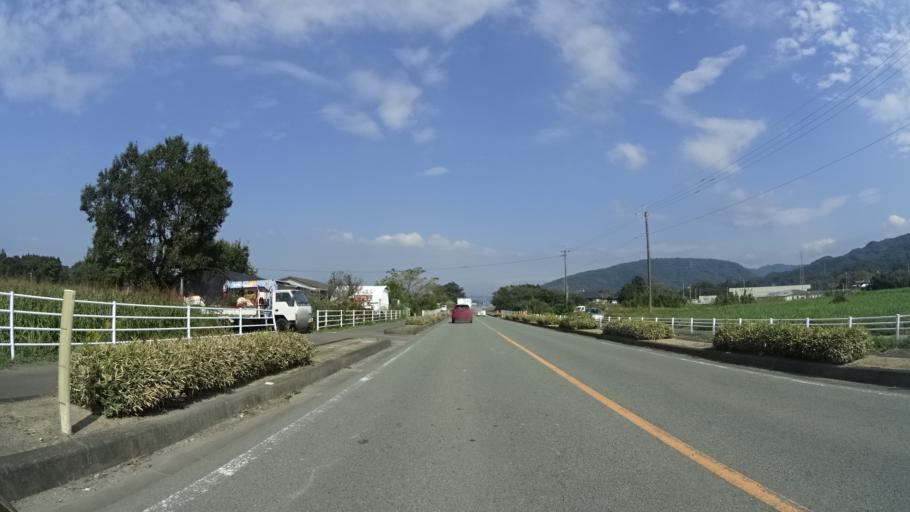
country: JP
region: Kumamoto
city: Kumamoto
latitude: 32.7513
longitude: 130.8016
